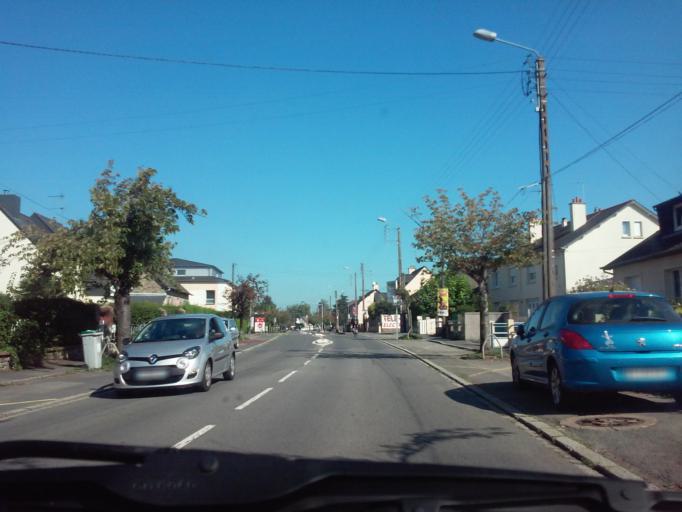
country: FR
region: Brittany
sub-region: Departement d'Ille-et-Vilaine
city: Betton
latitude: 48.1752
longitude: -1.6398
